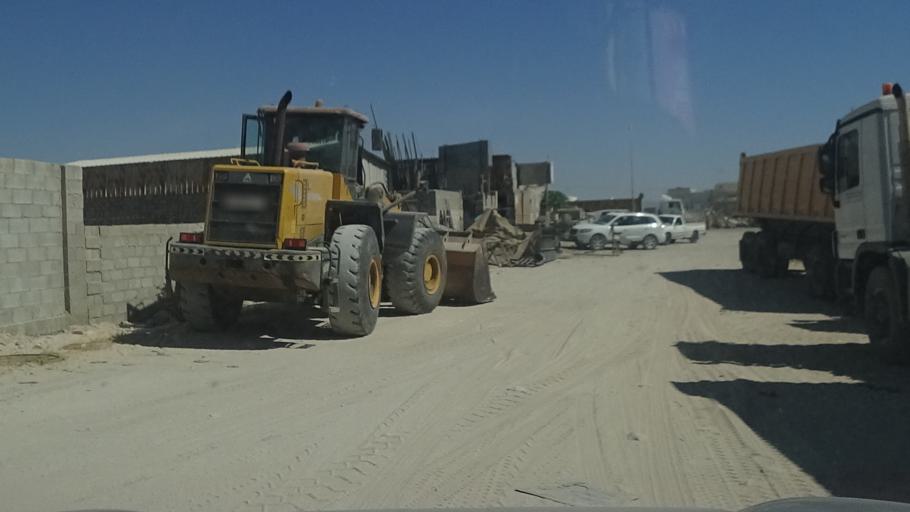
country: OM
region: Zufar
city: Salalah
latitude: 17.0326
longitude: 54.0419
